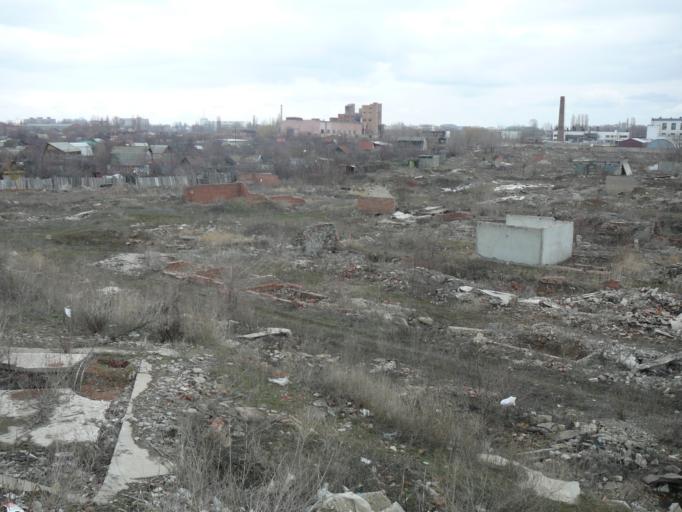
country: RU
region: Saratov
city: Engel's
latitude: 51.4628
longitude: 46.0956
